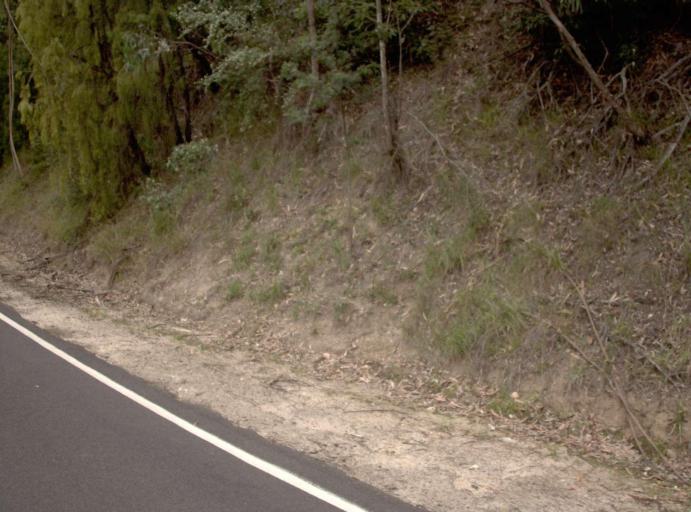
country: AU
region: New South Wales
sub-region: Bombala
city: Bombala
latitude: -37.4567
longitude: 149.1894
